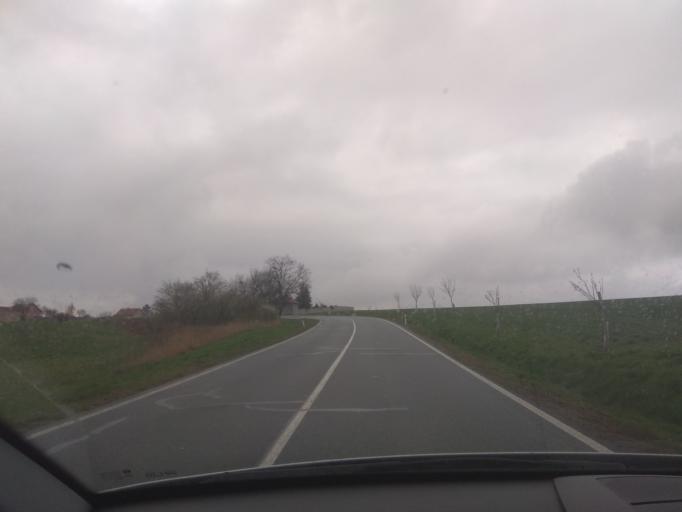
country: CZ
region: South Moravian
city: Zastavka
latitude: 49.1774
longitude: 16.3591
